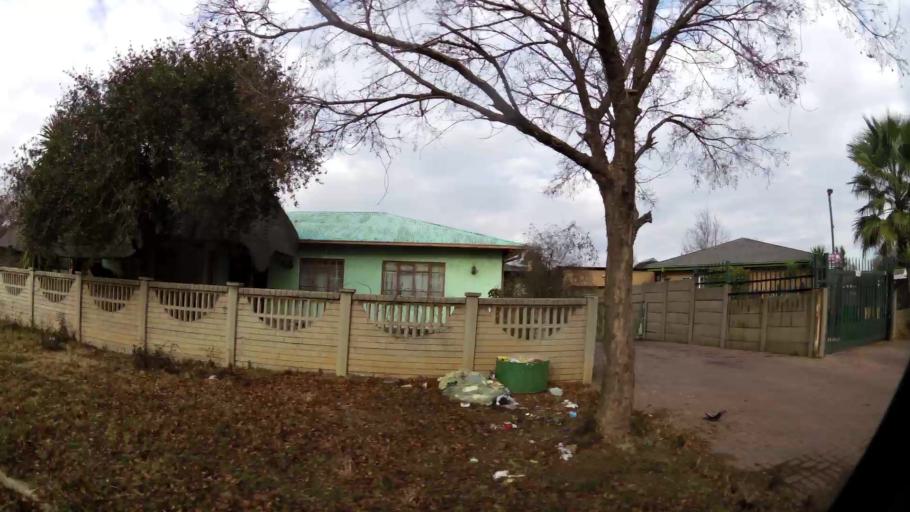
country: ZA
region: Gauteng
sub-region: Sedibeng District Municipality
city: Vanderbijlpark
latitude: -26.6944
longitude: 27.8156
